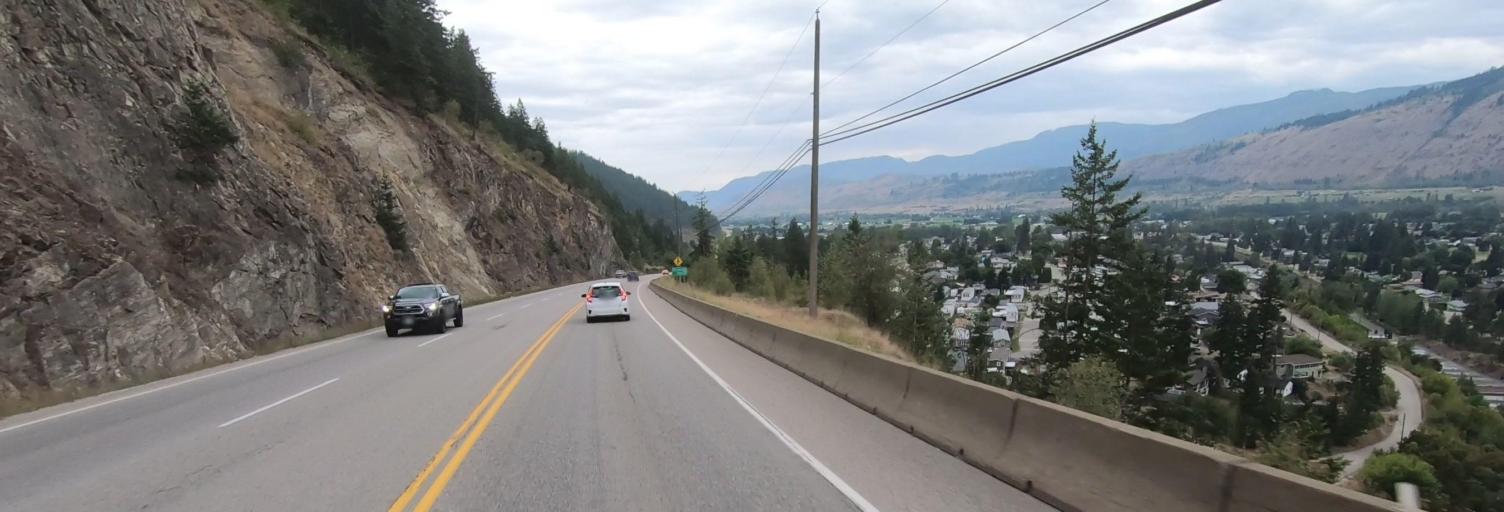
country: CA
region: British Columbia
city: Chase
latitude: 50.8246
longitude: -119.6724
